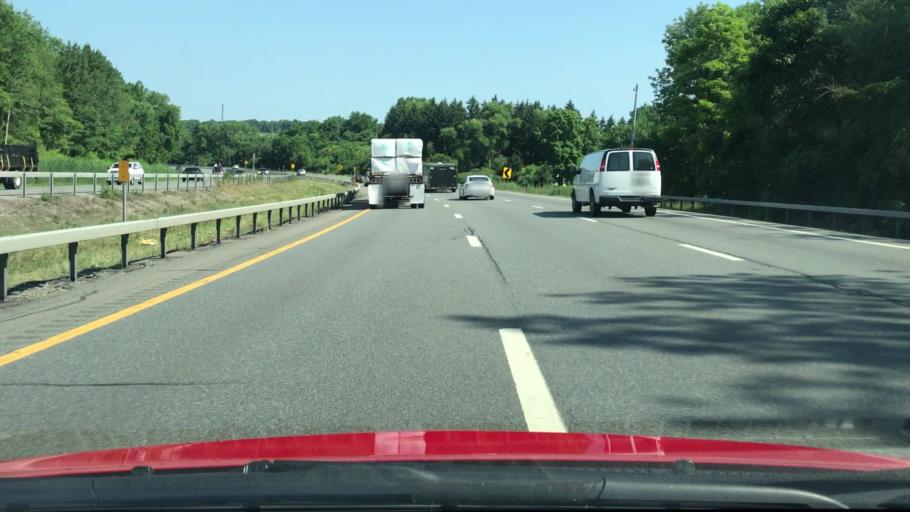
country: US
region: New York
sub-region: Albany County
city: Cohoes
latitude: 42.7861
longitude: -73.7578
